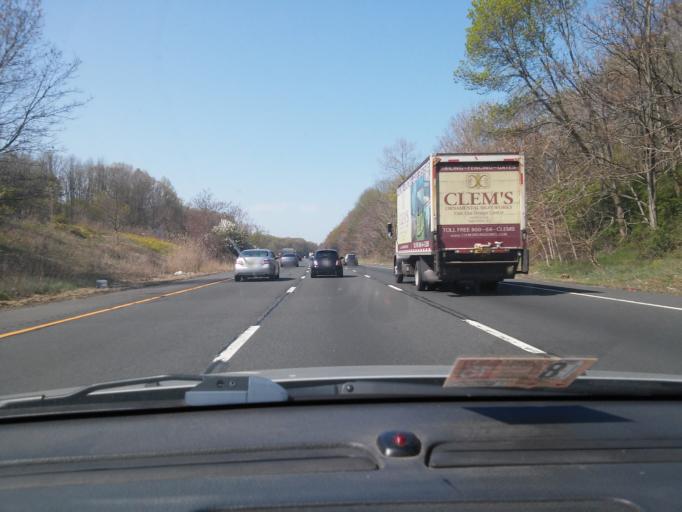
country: US
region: New Jersey
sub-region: Union County
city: Springfield
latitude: 40.7071
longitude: -74.3391
